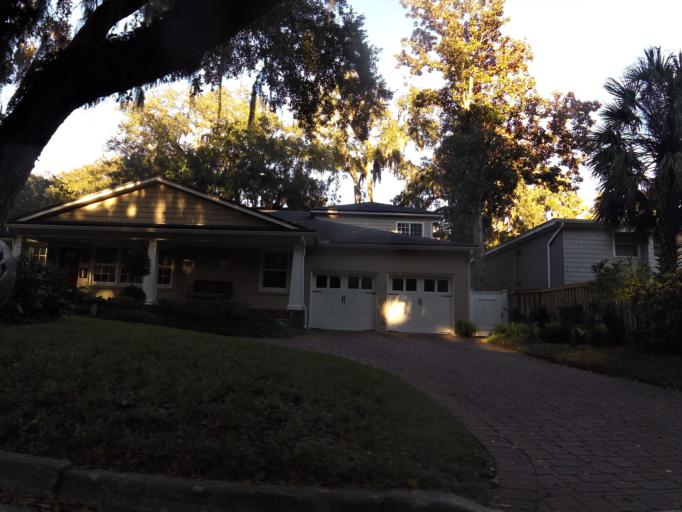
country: US
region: Florida
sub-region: Duval County
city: Jacksonville
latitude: 30.2703
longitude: -81.7047
